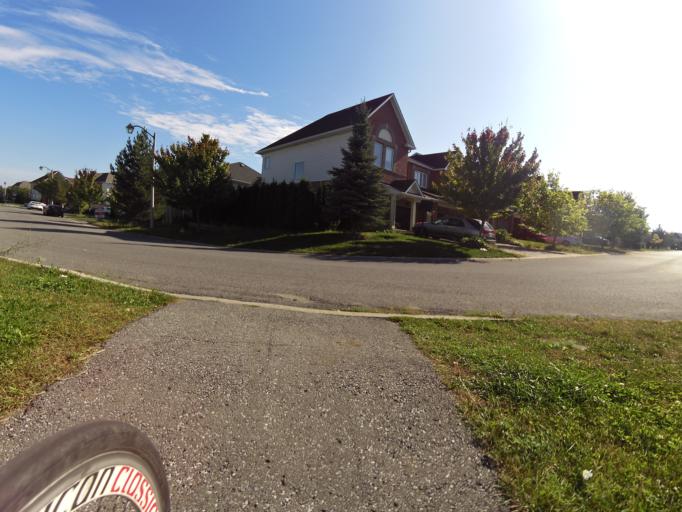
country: CA
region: Ontario
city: Bells Corners
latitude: 45.2711
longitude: -75.7088
